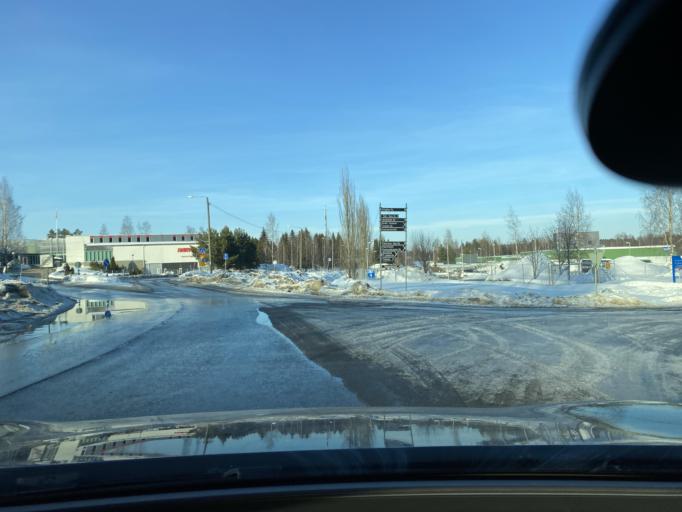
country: FI
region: Central Finland
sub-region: Jyvaeskylae
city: Muurame
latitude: 62.1019
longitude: 25.6482
